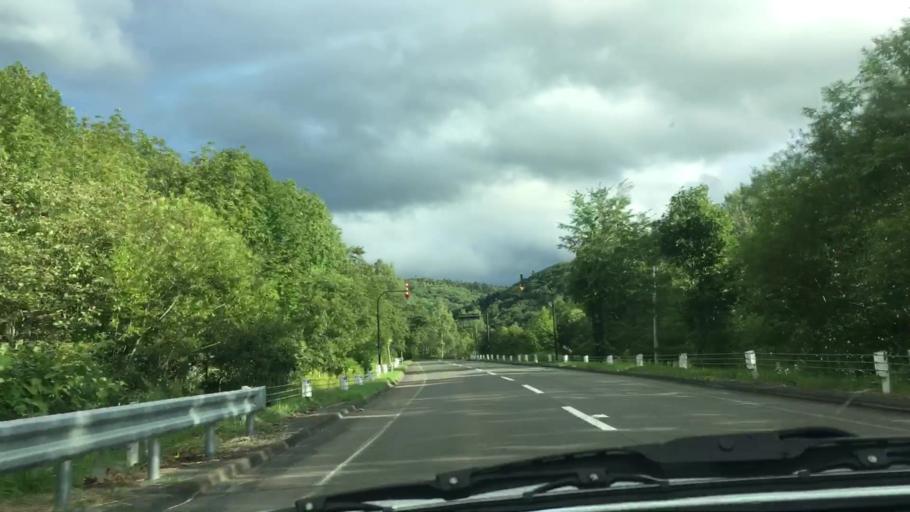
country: JP
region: Hokkaido
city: Shimo-furano
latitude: 43.1122
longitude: 142.6892
